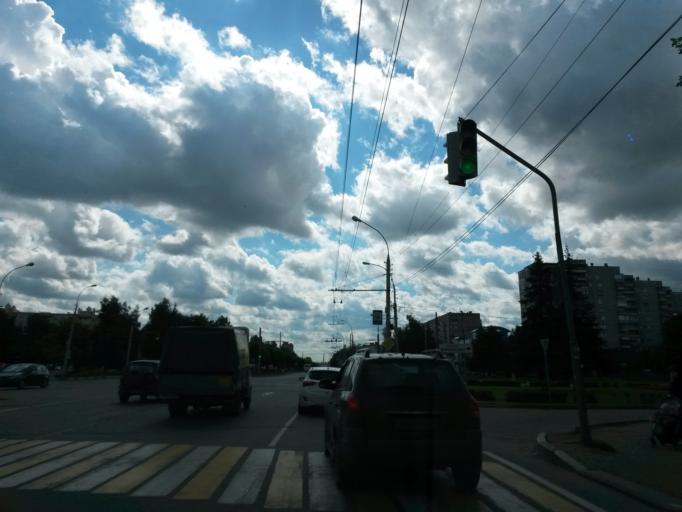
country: RU
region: Jaroslavl
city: Yaroslavl
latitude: 57.6860
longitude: 39.7840
